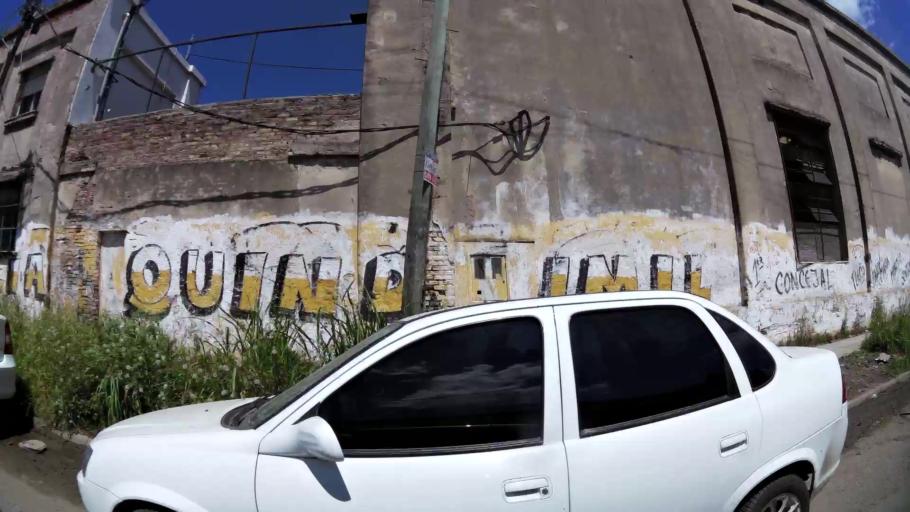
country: AR
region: Buenos Aires
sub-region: Partido de Lanus
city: Lanus
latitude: -34.6922
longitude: -58.4255
